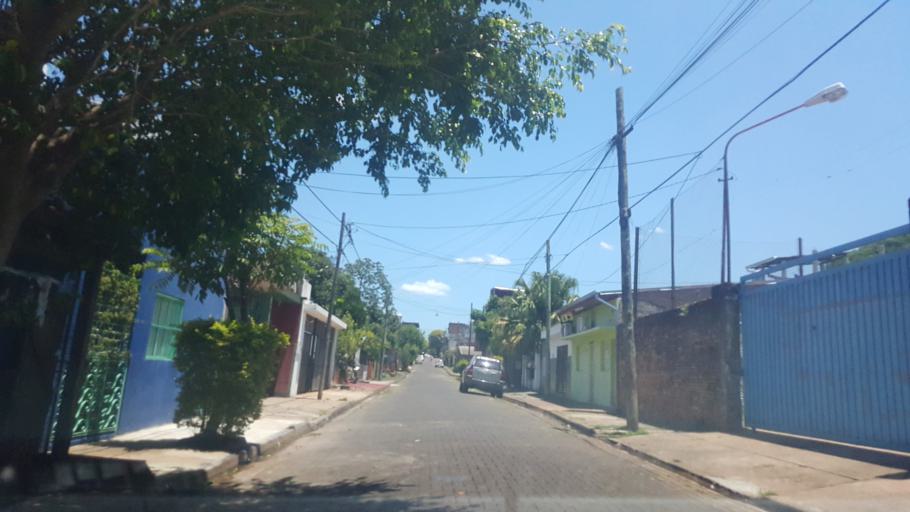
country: AR
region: Misiones
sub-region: Departamento de Capital
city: Posadas
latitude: -27.3680
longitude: -55.9042
